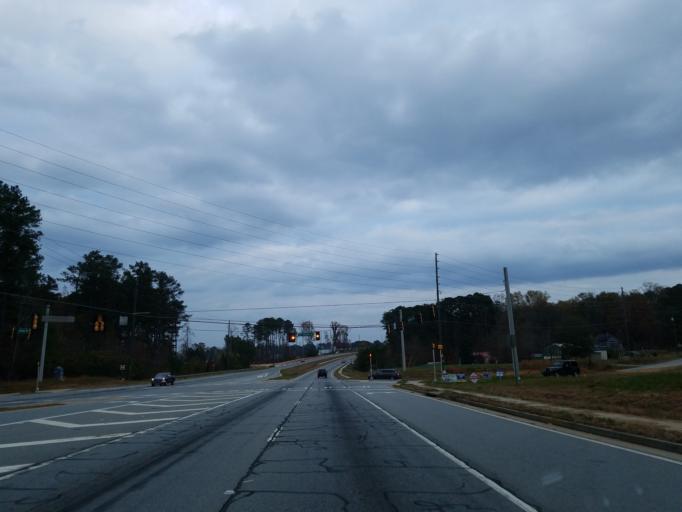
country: US
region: Georgia
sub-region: Cobb County
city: Acworth
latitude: 34.0972
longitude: -84.6387
